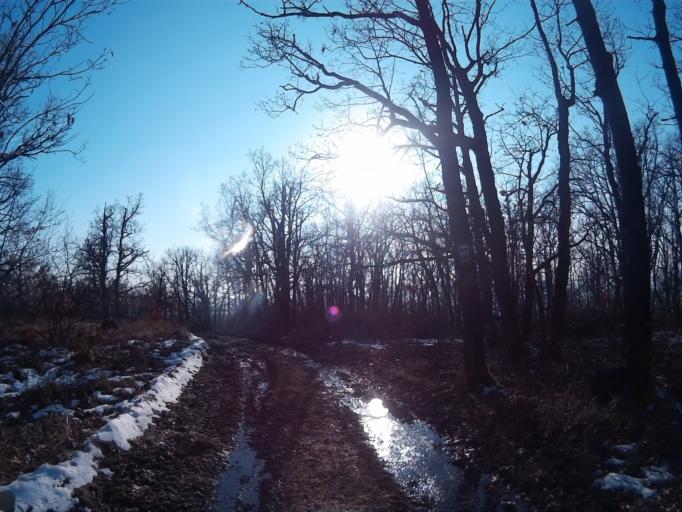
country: HU
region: Nograd
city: Paszto
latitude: 47.9425
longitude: 19.6327
